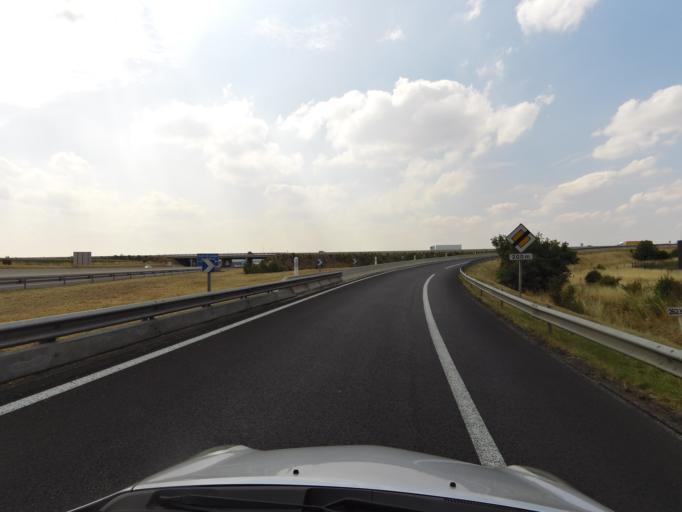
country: FR
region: Champagne-Ardenne
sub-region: Departement de la Marne
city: Tinqueux
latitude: 49.2516
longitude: 3.9633
